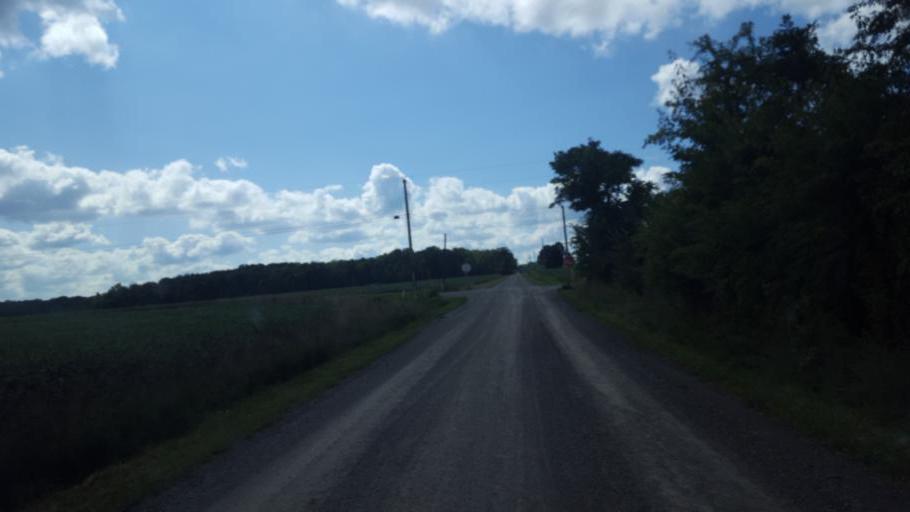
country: US
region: Ohio
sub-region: Wayne County
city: West Salem
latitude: 41.0565
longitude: -82.0961
